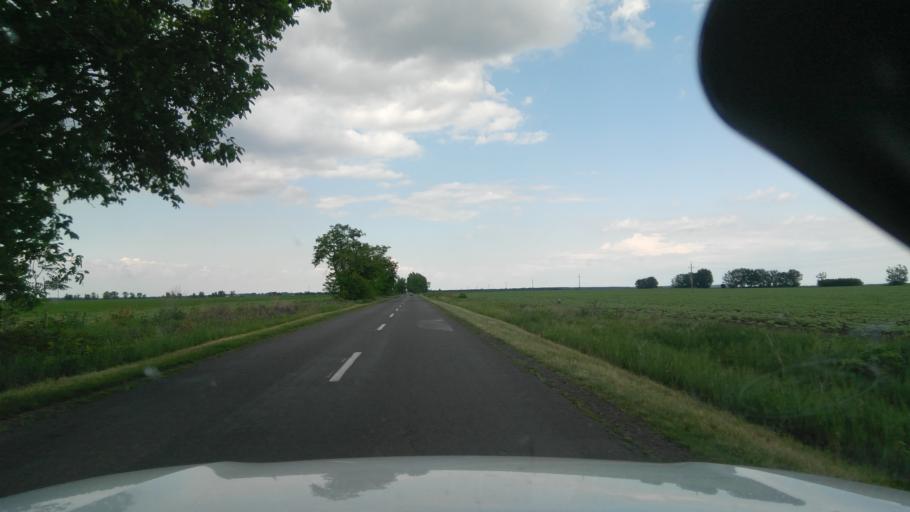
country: HU
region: Bekes
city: Magyarbanhegyes
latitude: 46.4495
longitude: 20.9933
